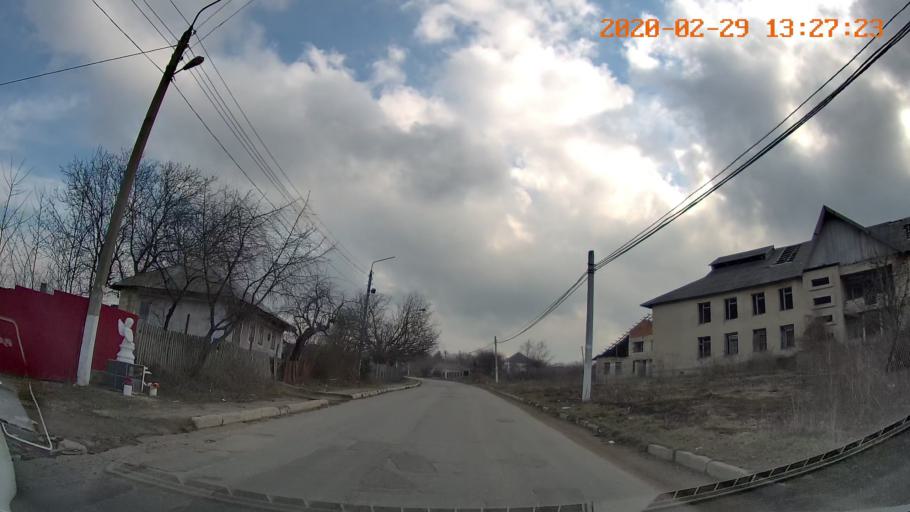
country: MD
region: Telenesti
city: Camenca
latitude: 47.9122
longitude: 28.6409
